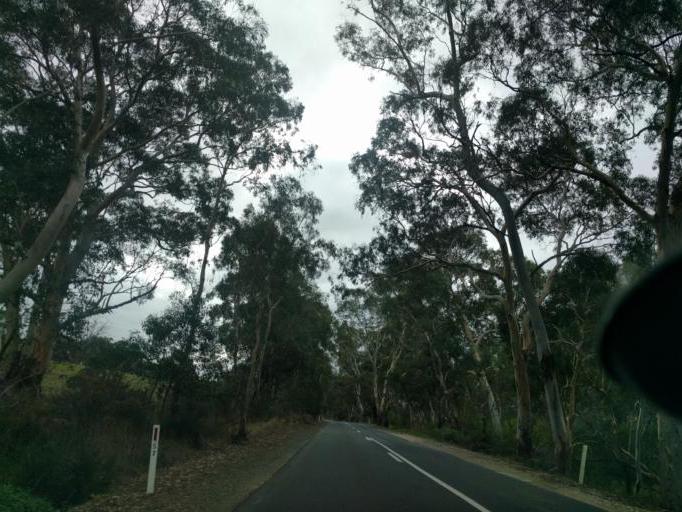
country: AU
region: South Australia
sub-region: Mount Barker
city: Hahndorf
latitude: -35.0653
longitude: 138.7714
